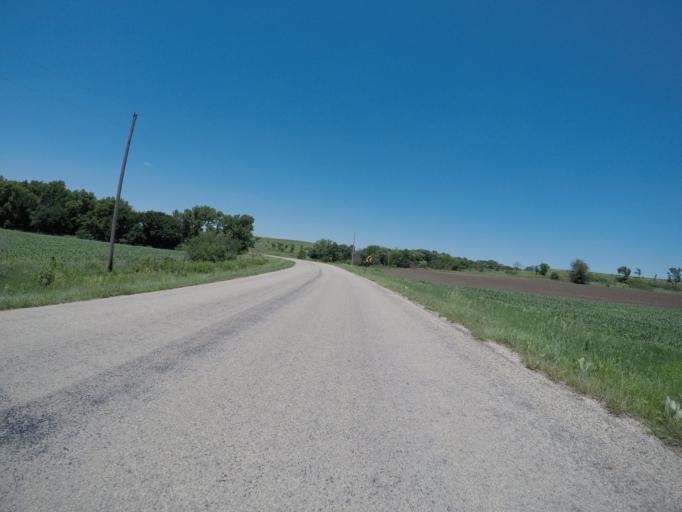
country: US
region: Kansas
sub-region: Geary County
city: Grandview Plaza
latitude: 38.8568
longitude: -96.7793
